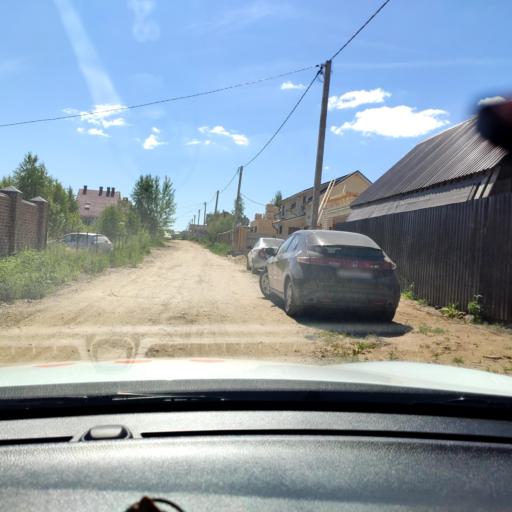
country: RU
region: Tatarstan
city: Vysokaya Gora
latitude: 55.8172
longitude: 49.2884
